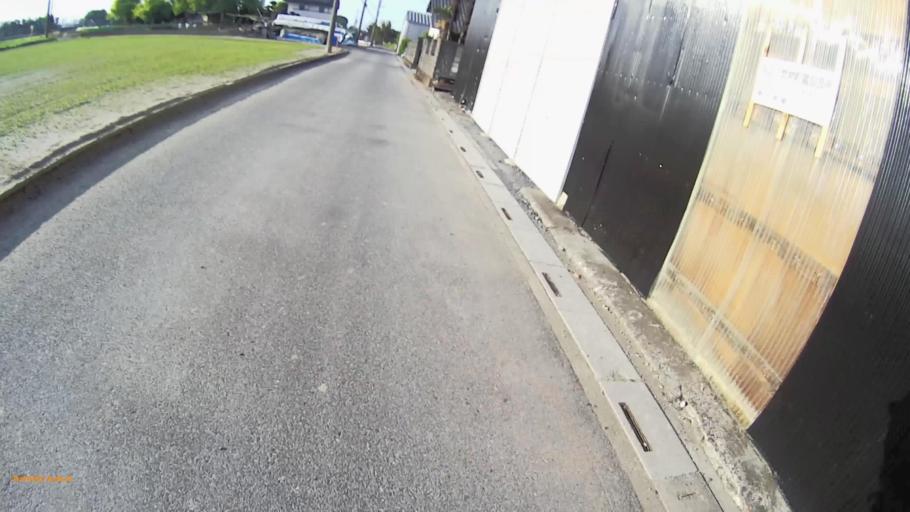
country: JP
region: Saitama
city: Satte
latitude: 36.1028
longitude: 139.7225
